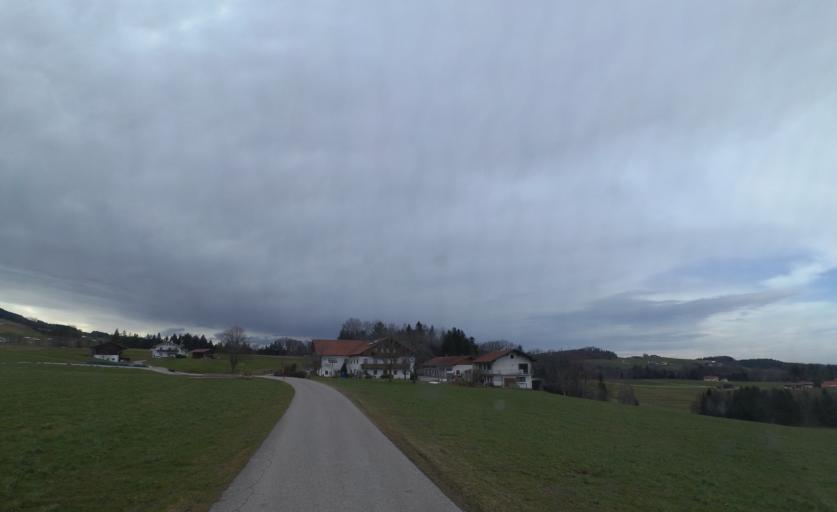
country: DE
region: Bavaria
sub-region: Upper Bavaria
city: Teisendorf
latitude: 47.8289
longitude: 12.7865
